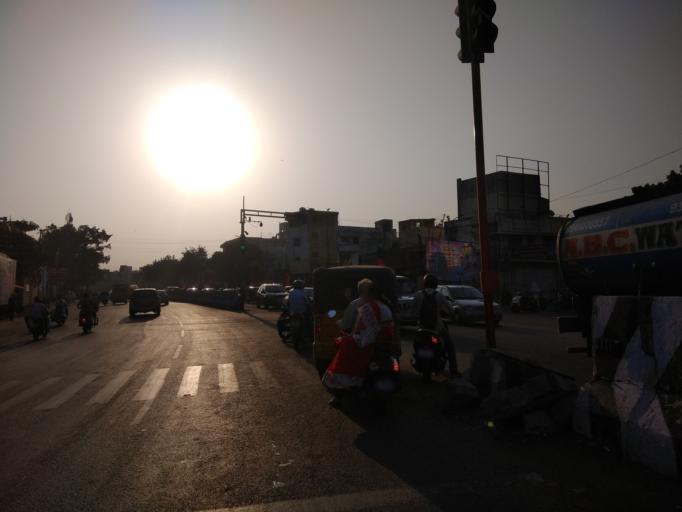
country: IN
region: Tamil Nadu
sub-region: Chennai
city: Chetput
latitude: 13.0769
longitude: 80.2120
